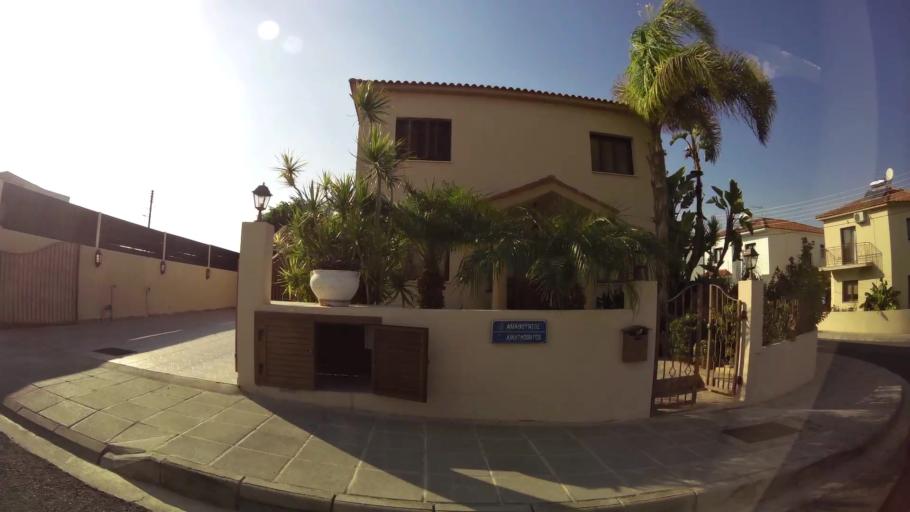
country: CY
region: Larnaka
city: Aradippou
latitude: 34.9460
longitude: 33.6012
